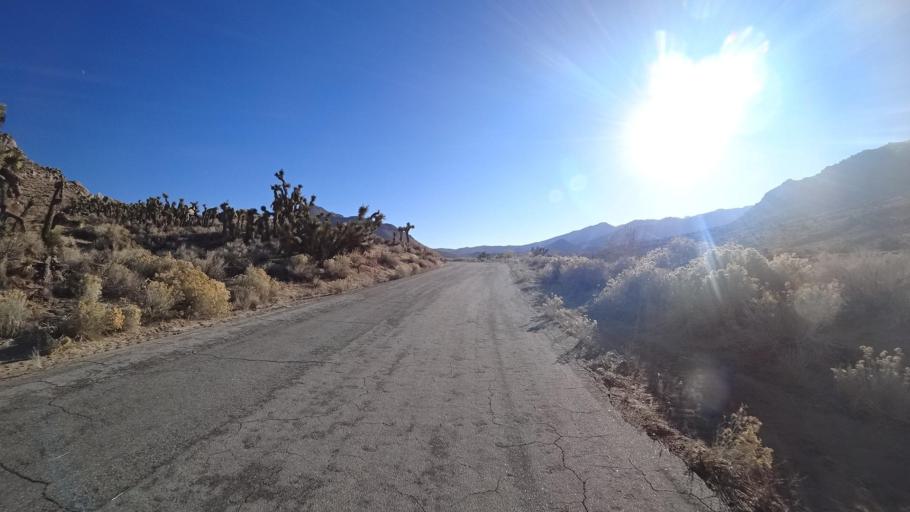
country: US
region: California
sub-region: Kern County
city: Weldon
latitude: 35.4971
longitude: -118.2043
